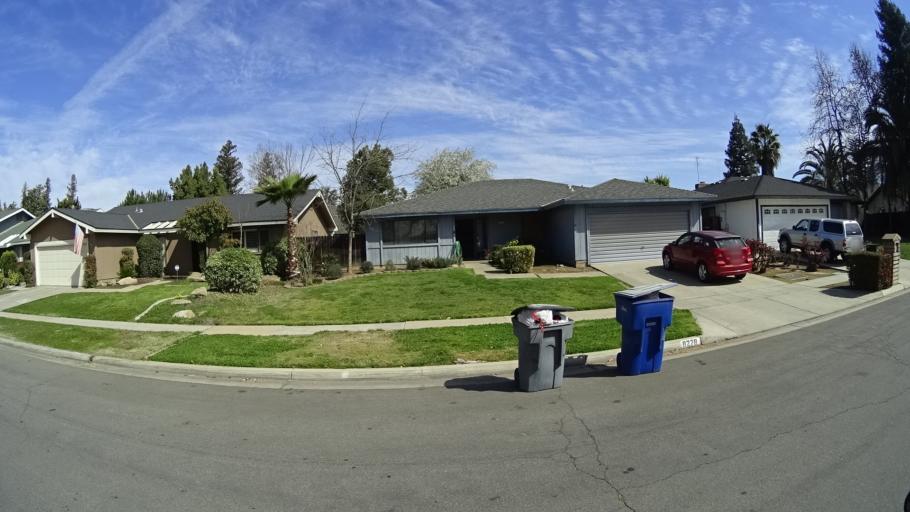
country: US
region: California
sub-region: Fresno County
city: Clovis
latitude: 36.8561
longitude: -119.7768
